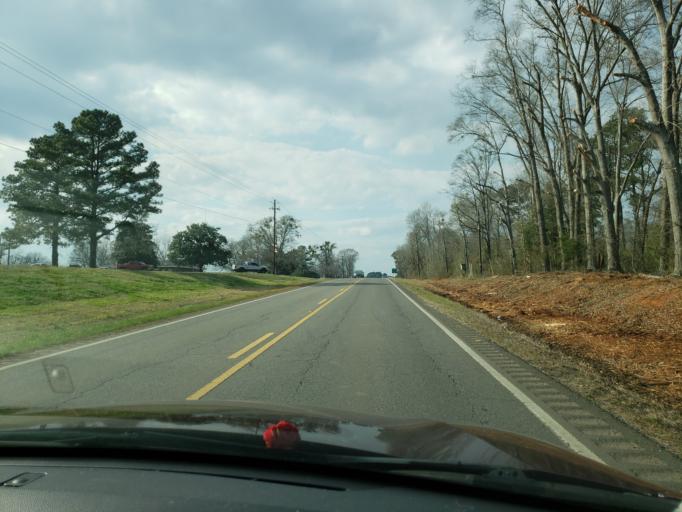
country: US
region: Alabama
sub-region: Hale County
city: Greensboro
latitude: 32.7123
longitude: -87.6137
